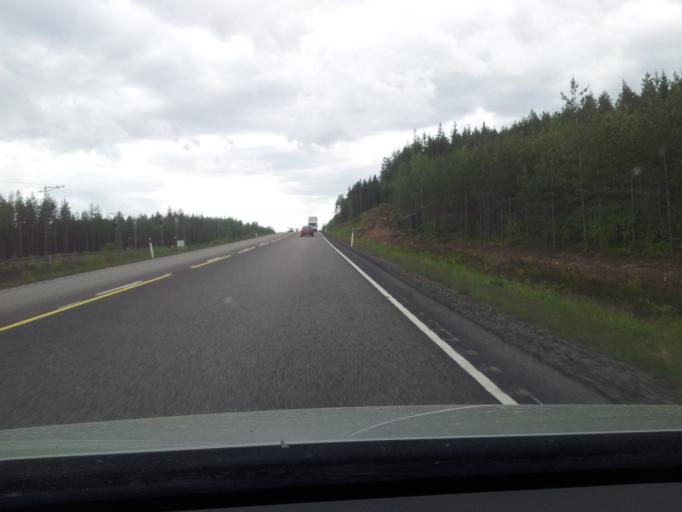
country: FI
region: South Karelia
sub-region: Lappeenranta
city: Taavetti
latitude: 60.9058
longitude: 27.2357
